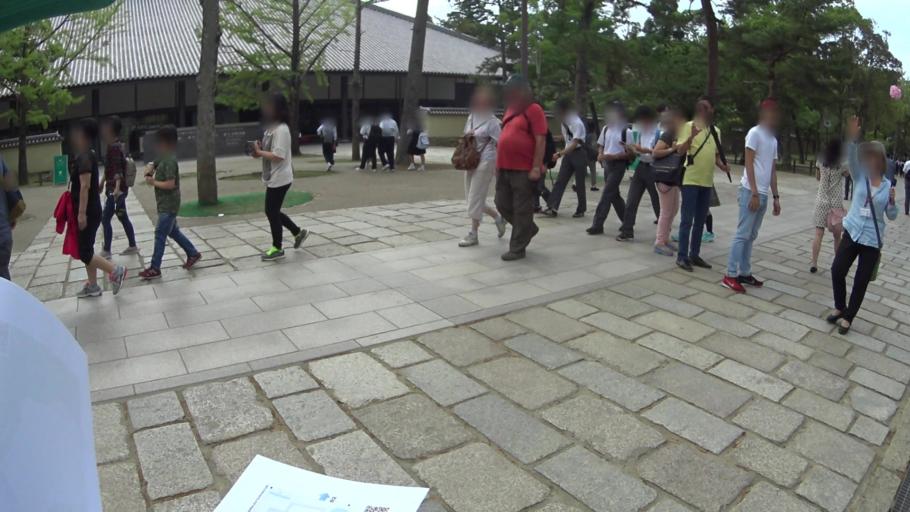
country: JP
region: Nara
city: Nara-shi
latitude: 34.6862
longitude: 135.8399
